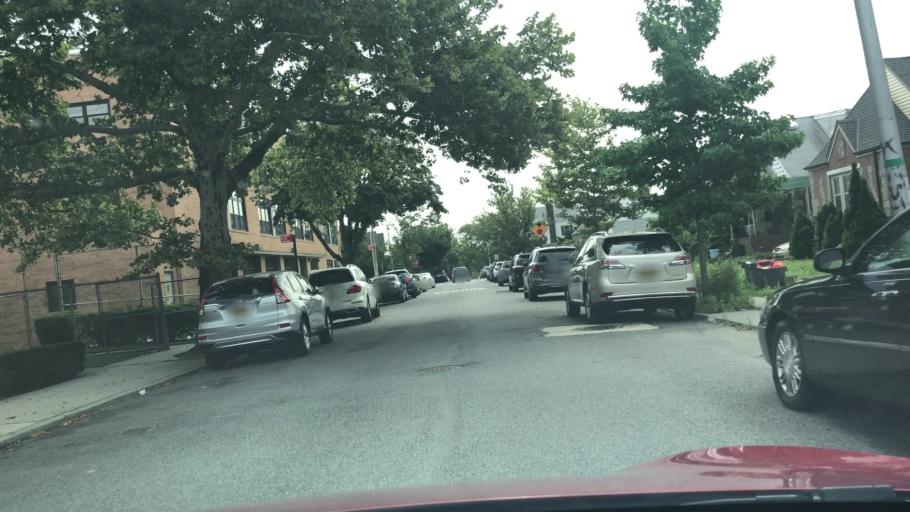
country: US
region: New York
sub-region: Queens County
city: Jamaica
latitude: 40.7442
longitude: -73.8234
